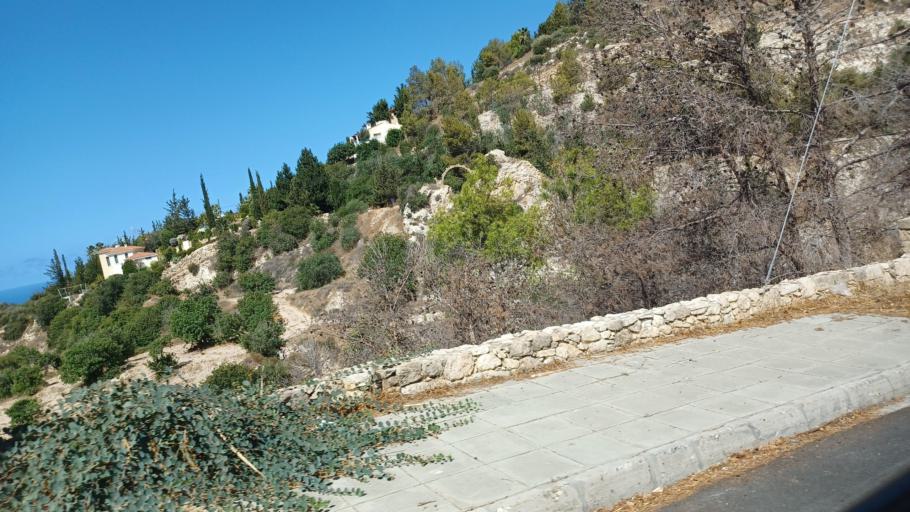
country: CY
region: Pafos
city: Tala
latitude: 34.8485
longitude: 32.4302
